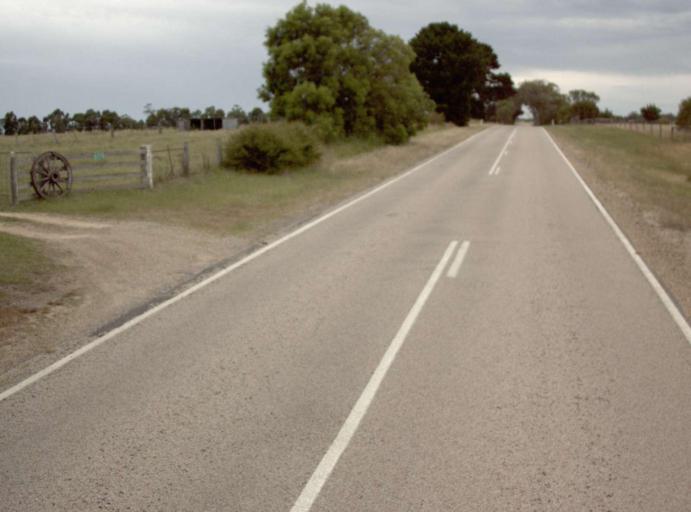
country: AU
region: Victoria
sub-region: East Gippsland
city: Bairnsdale
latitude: -37.9246
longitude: 147.5447
